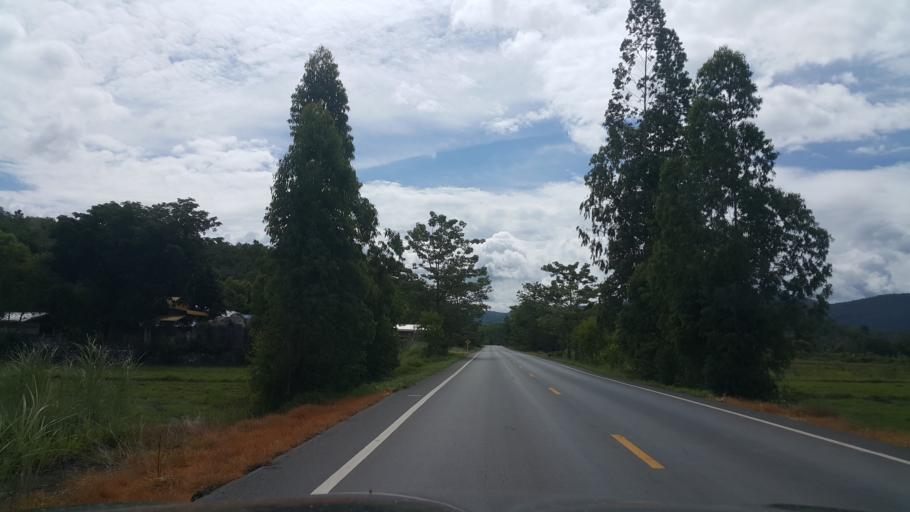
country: TH
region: Uttaradit
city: Thong Saen Khan
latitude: 17.3639
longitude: 100.2423
